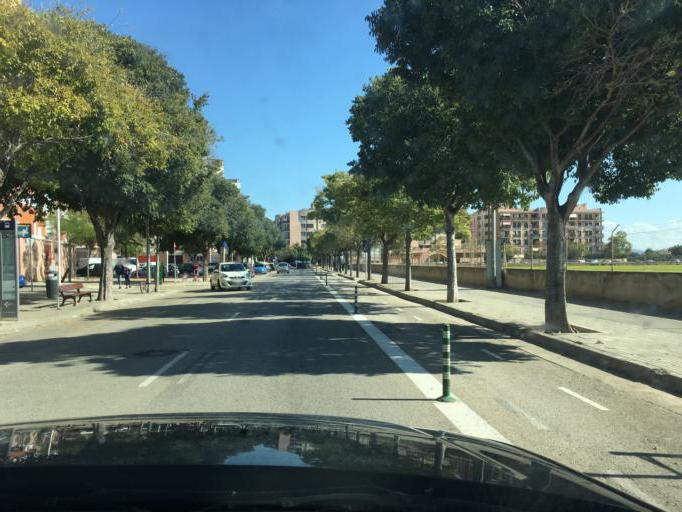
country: ES
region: Balearic Islands
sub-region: Illes Balears
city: Palma
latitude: 39.5821
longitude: 2.6808
